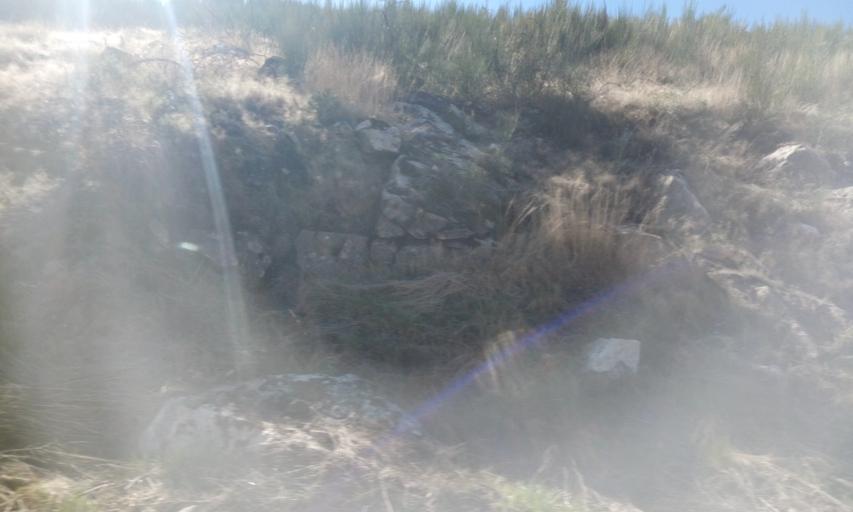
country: PT
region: Guarda
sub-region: Manteigas
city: Manteigas
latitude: 40.4953
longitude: -7.5275
